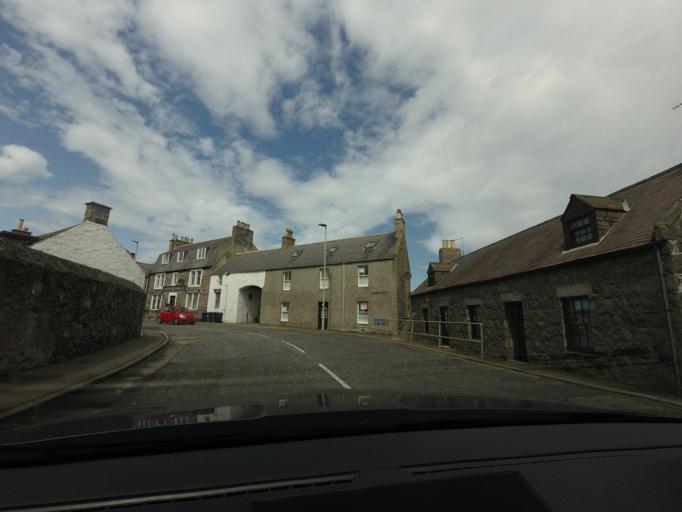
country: GB
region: Scotland
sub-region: Aberdeenshire
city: Portsoy
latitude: 57.6813
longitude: -2.6870
